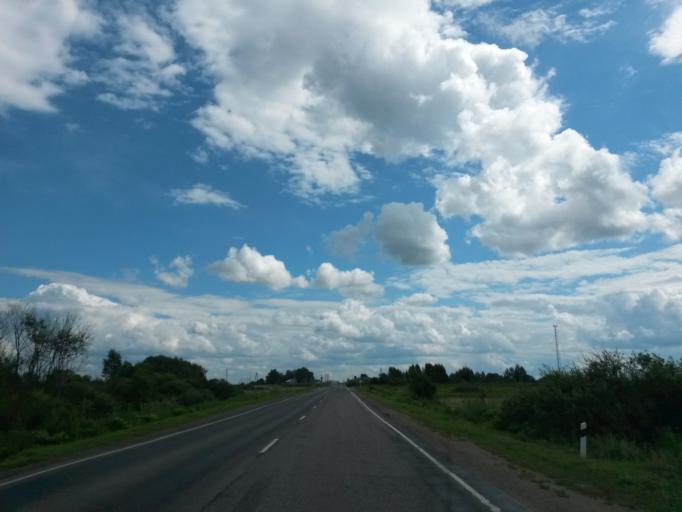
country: RU
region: Jaroslavl
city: Dubki
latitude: 57.2034
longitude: 40.3247
